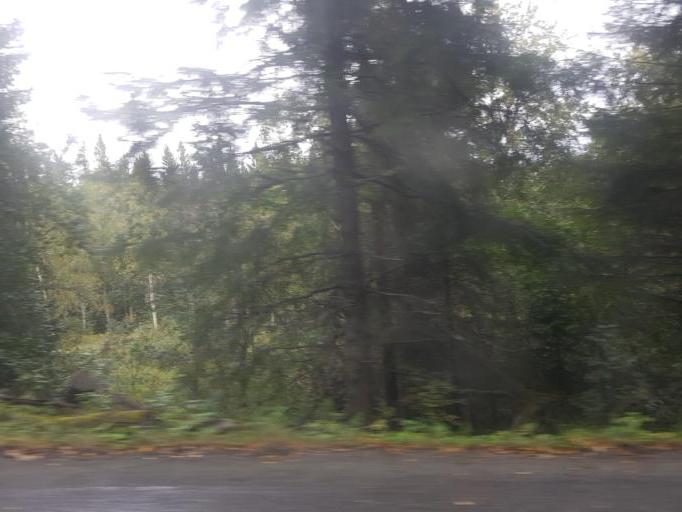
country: NO
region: Sor-Trondelag
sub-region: Trondheim
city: Trondheim
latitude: 63.4166
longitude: 10.3208
